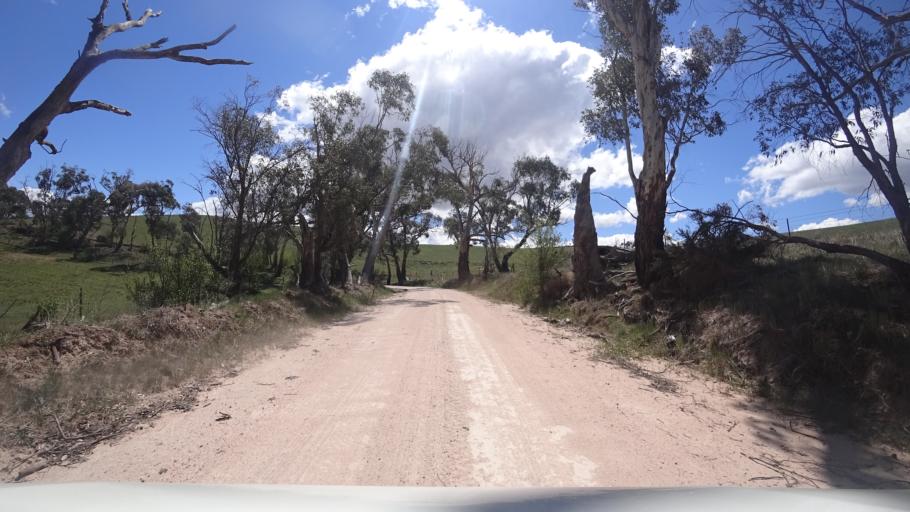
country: AU
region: New South Wales
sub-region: Oberon
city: Oberon
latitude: -33.5631
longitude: 149.9405
